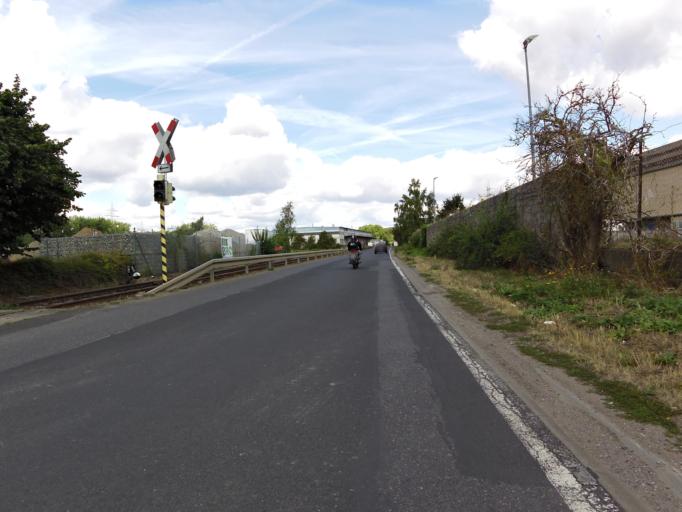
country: DE
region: Bavaria
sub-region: Regierungsbezirk Unterfranken
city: Zell am Main
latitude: 49.8148
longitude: 9.8756
